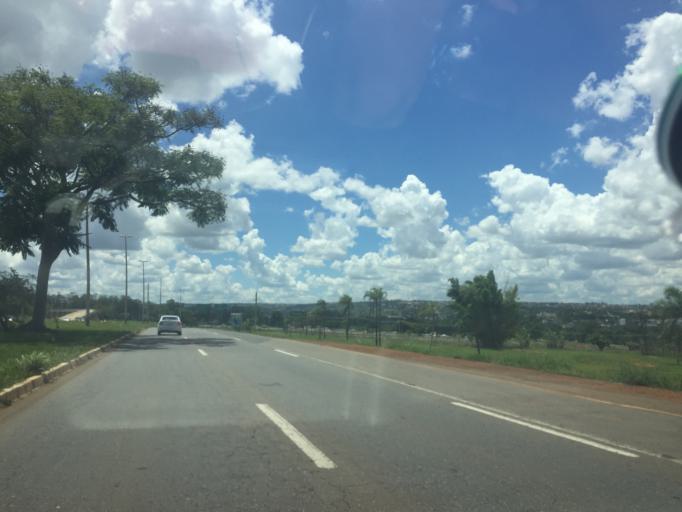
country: BR
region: Federal District
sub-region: Brasilia
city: Brasilia
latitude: -15.8733
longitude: -47.9545
